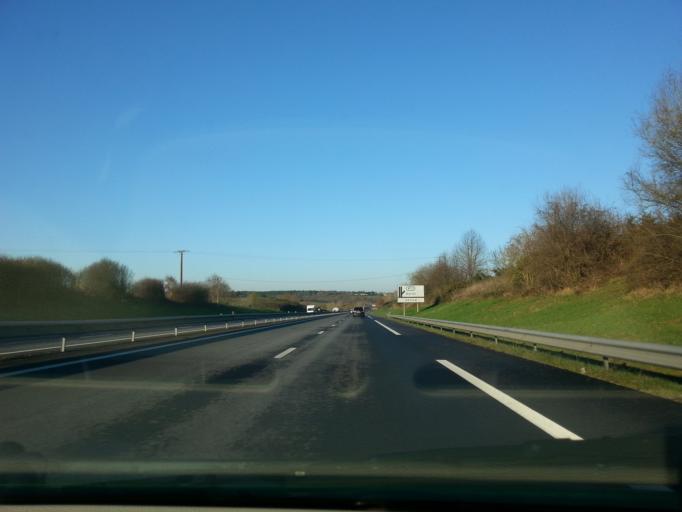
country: FR
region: Pays de la Loire
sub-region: Departement de Maine-et-Loire
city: Durtal
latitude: 47.6458
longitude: -0.2739
